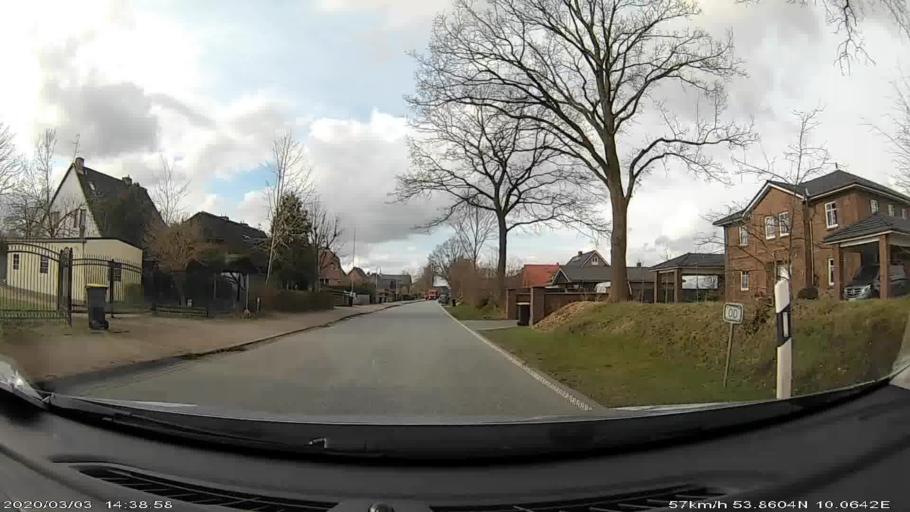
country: DE
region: Schleswig-Holstein
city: Struvenhutten
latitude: 53.8606
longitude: 10.0641
